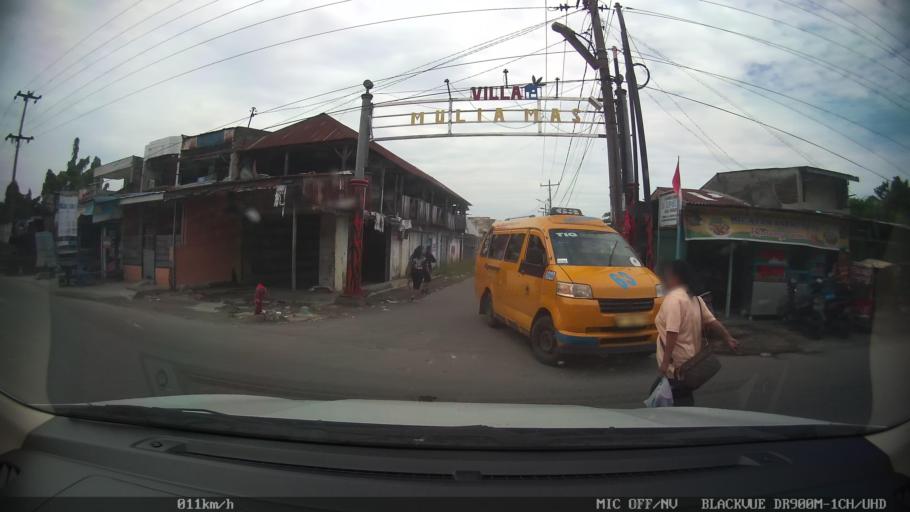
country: ID
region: North Sumatra
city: Sunggal
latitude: 3.6007
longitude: 98.5901
